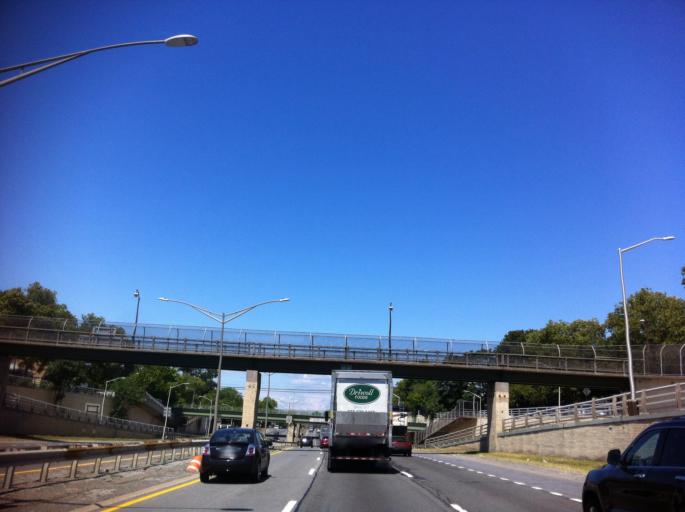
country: US
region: New York
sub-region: Nassau County
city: Bellerose Terrace
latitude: 40.7346
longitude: -73.7669
